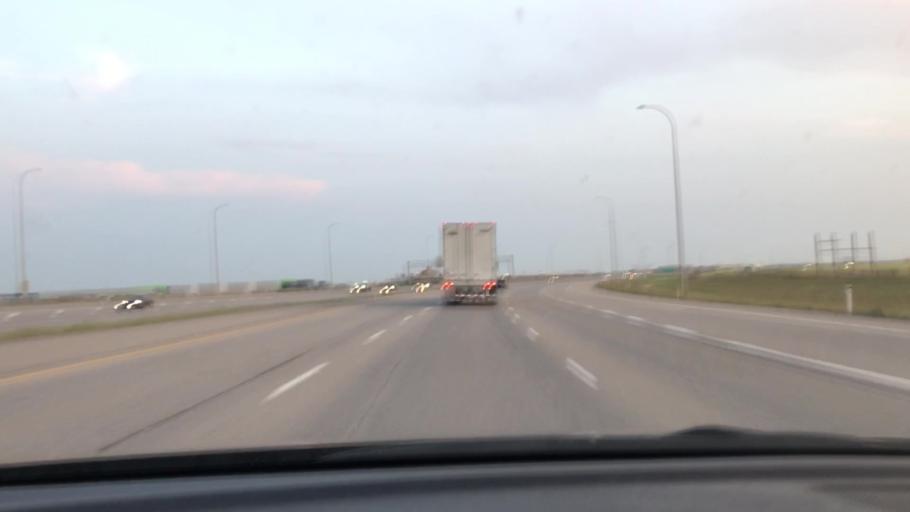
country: CA
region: Alberta
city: Airdrie
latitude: 51.1684
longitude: -114.0021
